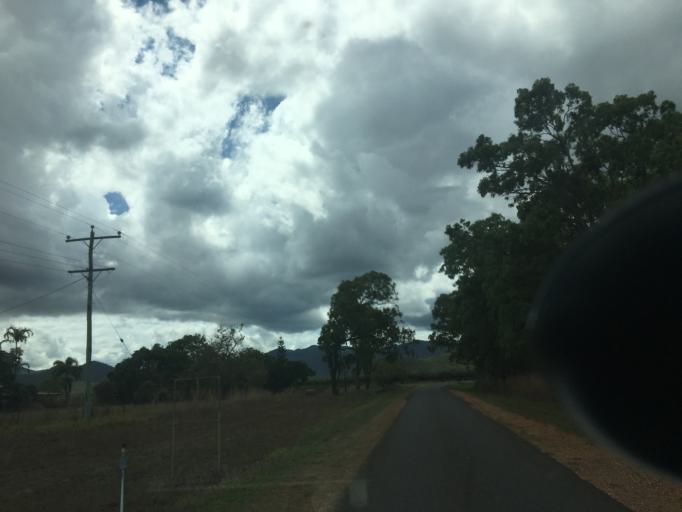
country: AU
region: Queensland
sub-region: Tablelands
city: Mareeba
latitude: -16.9997
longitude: 145.5259
